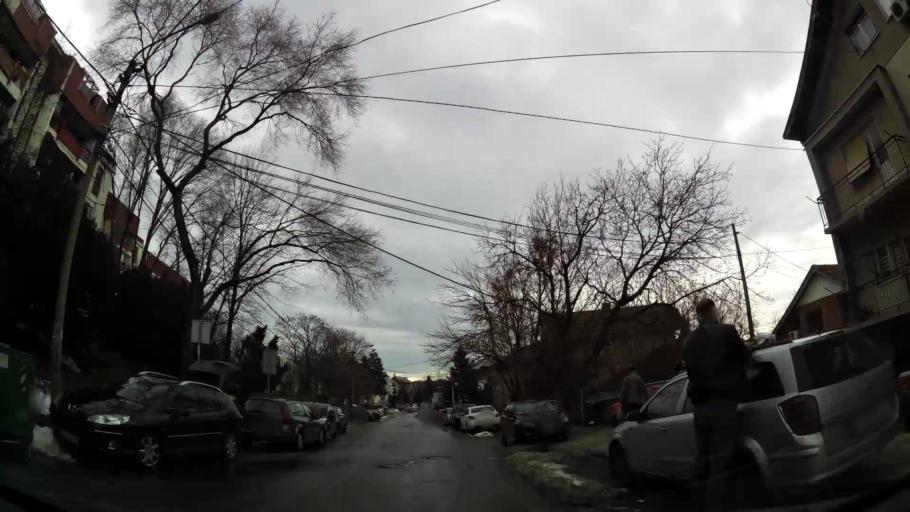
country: RS
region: Central Serbia
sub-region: Belgrade
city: Rakovica
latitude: 44.7514
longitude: 20.4173
